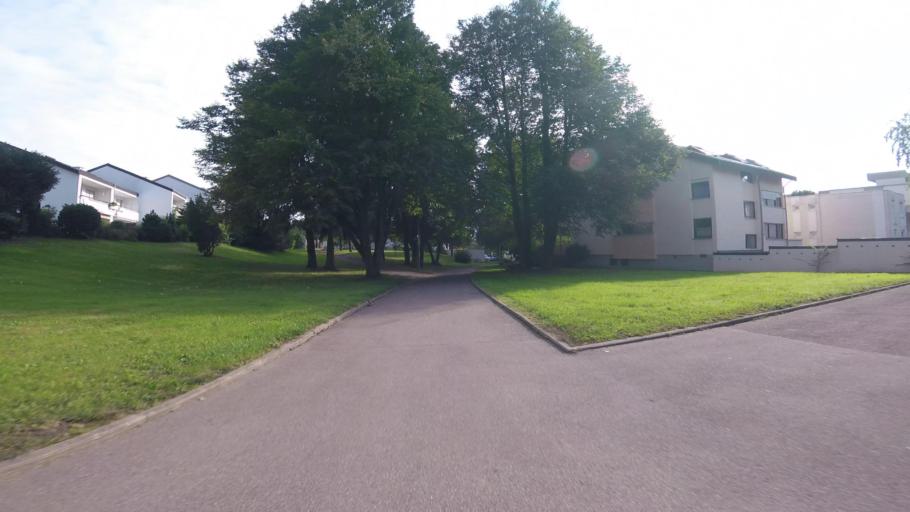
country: DE
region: Baden-Wuerttemberg
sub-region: Regierungsbezirk Stuttgart
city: Backnang
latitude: 48.9536
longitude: 9.4226
